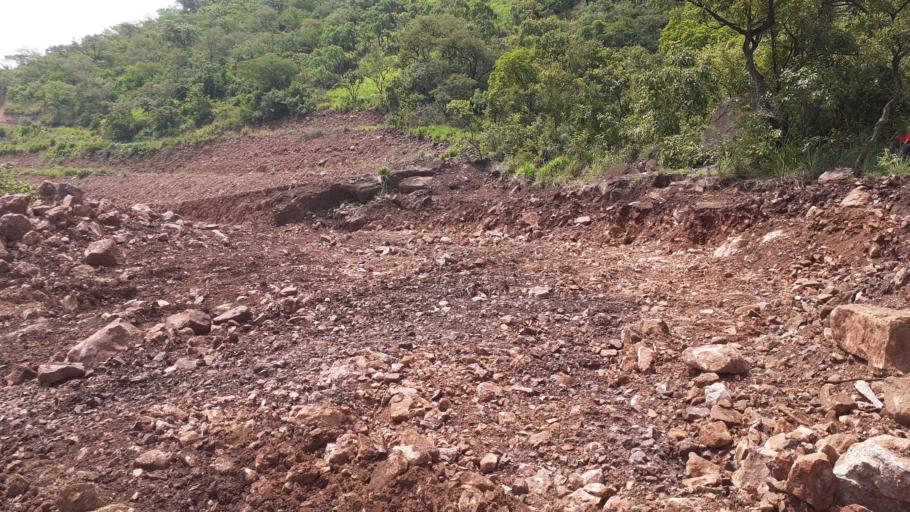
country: ET
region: Southern Nations, Nationalities, and People's Region
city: Areka
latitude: 7.6159
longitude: 37.5197
